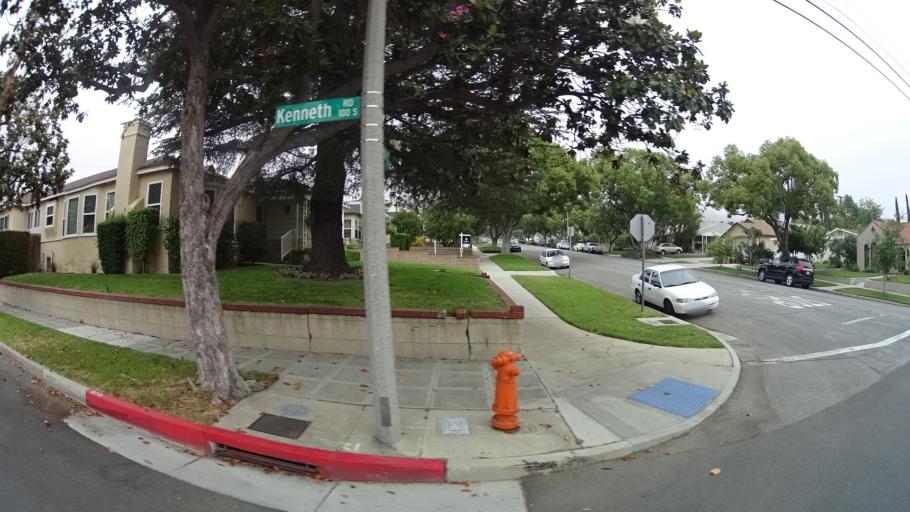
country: US
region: California
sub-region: Los Angeles County
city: Burbank
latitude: 34.1871
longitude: -118.3004
